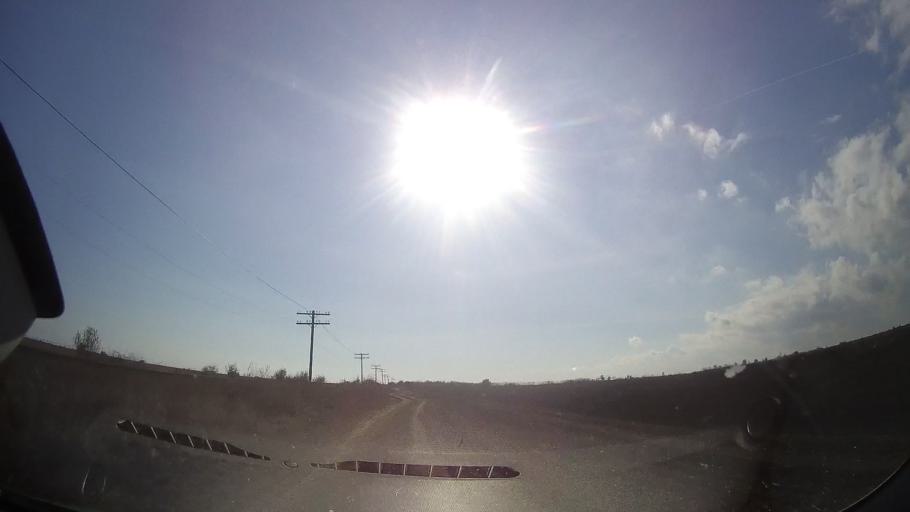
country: RO
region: Constanta
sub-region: Comuna Tuzla
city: Tuzla
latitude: 43.9777
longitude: 28.6442
